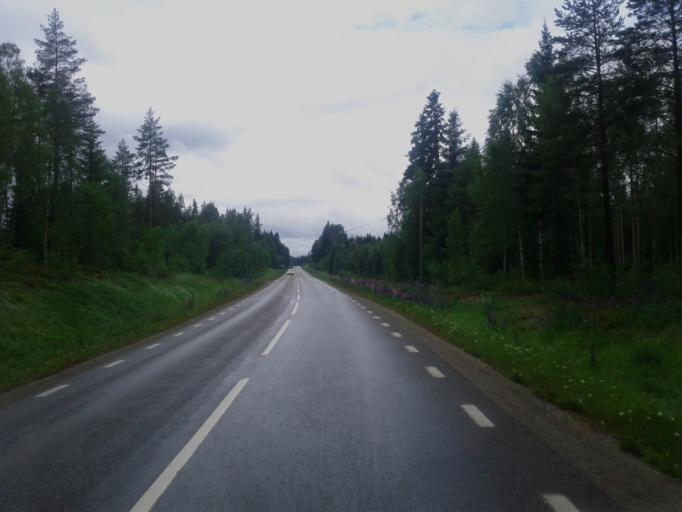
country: SE
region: Gaevleborg
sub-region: Nordanstigs Kommun
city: Bergsjoe
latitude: 62.0970
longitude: 16.7588
